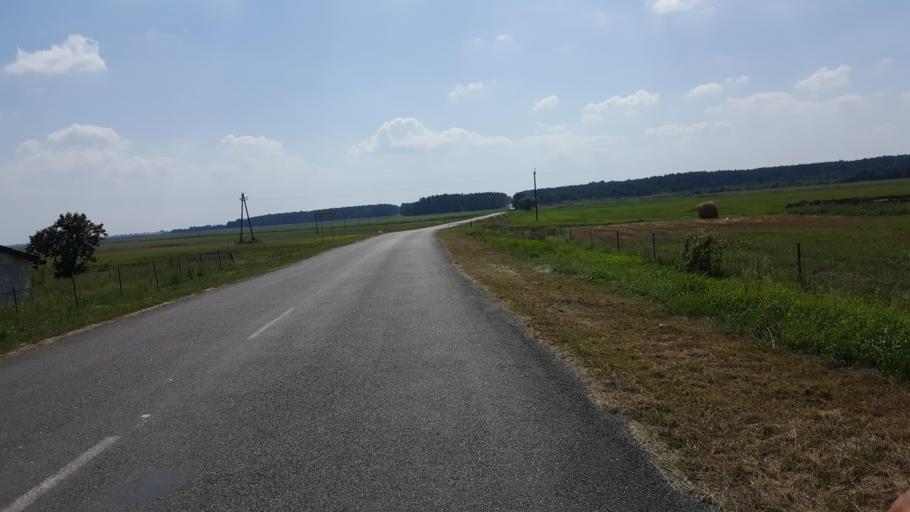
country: PL
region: Podlasie
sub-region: Powiat hajnowski
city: Czeremcha
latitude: 52.5361
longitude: 23.5361
